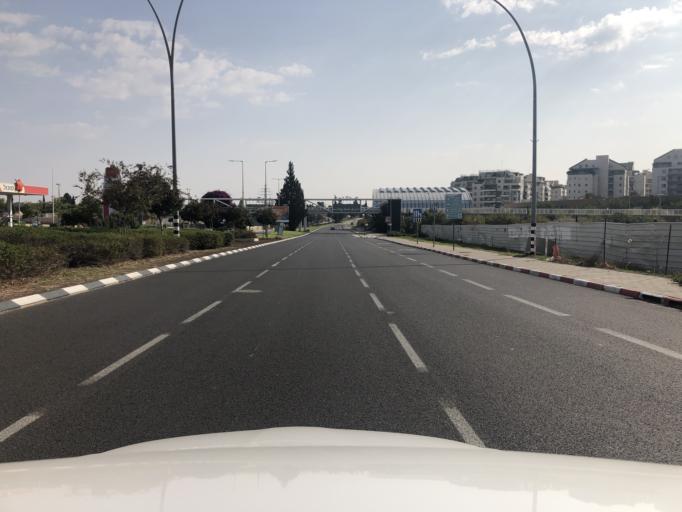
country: IL
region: Central District
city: Ra'anana
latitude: 32.1912
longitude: 34.8915
